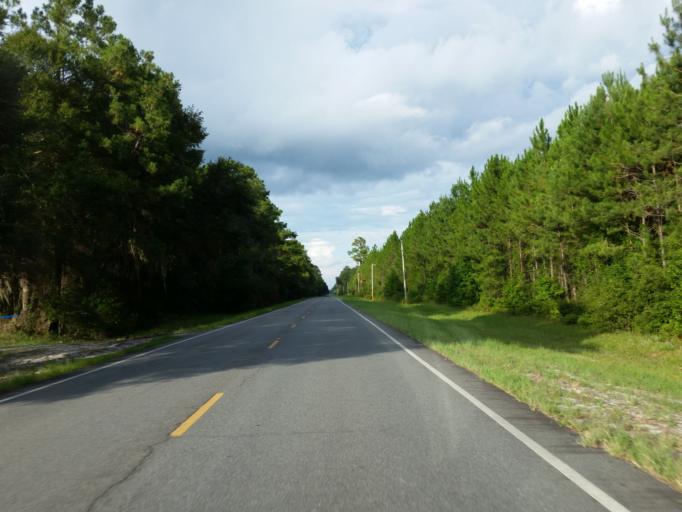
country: US
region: Florida
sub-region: Hamilton County
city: Jasper
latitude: 30.6212
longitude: -82.6193
